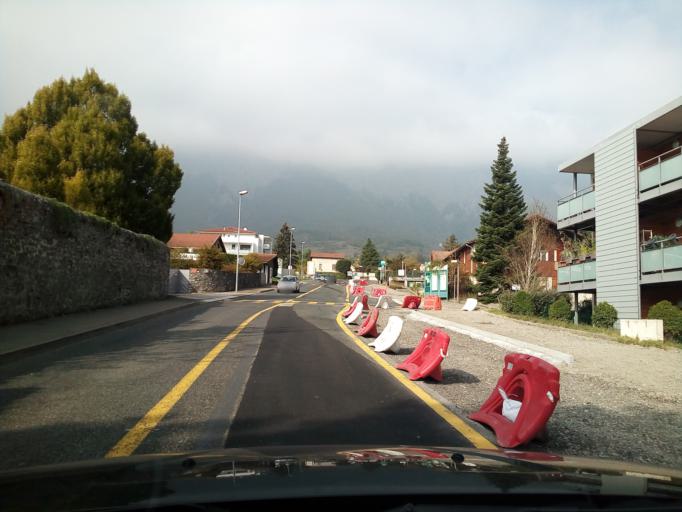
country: FR
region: Rhone-Alpes
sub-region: Departement de l'Isere
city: Saint-Ismier
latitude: 45.2429
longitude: 5.8288
